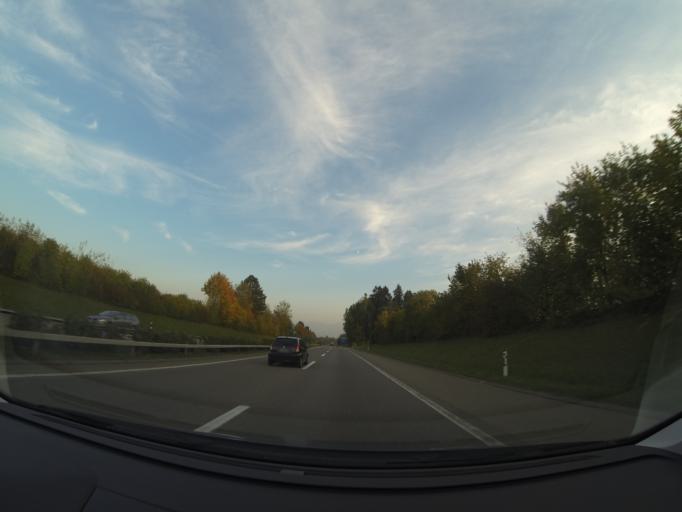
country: CH
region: Zurich
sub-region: Bezirk Hinwil
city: Bubikon
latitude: 47.2807
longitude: 8.8244
